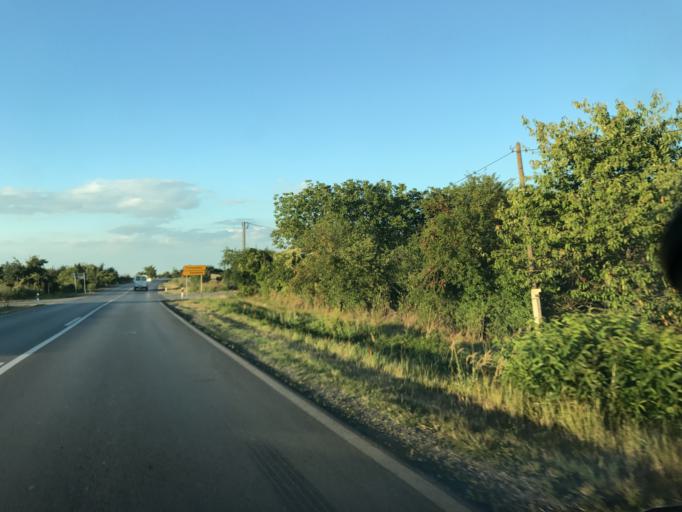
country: RS
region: Central Serbia
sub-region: Branicevski Okrug
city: Pozarevac
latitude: 44.6359
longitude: 21.1477
